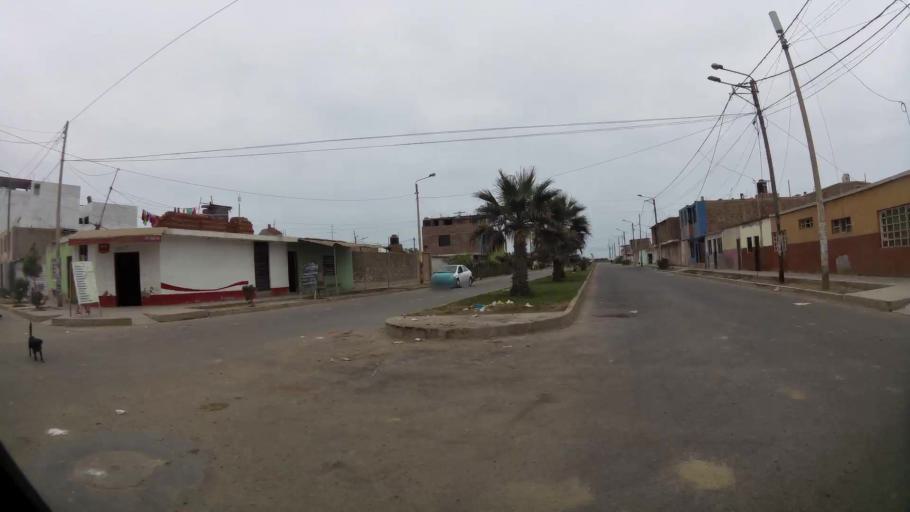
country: PE
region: La Libertad
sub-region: Provincia de Trujillo
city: Buenos Aires
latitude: -8.1459
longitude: -79.0512
